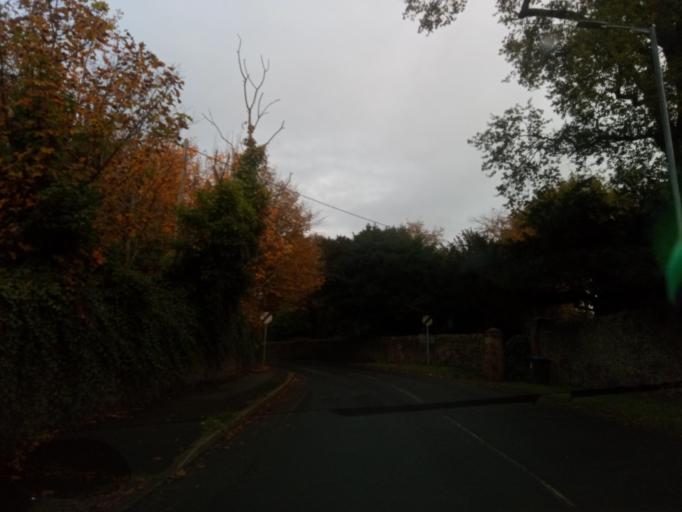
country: GB
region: Scotland
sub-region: The Scottish Borders
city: Eyemouth
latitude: 55.8436
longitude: -2.1205
